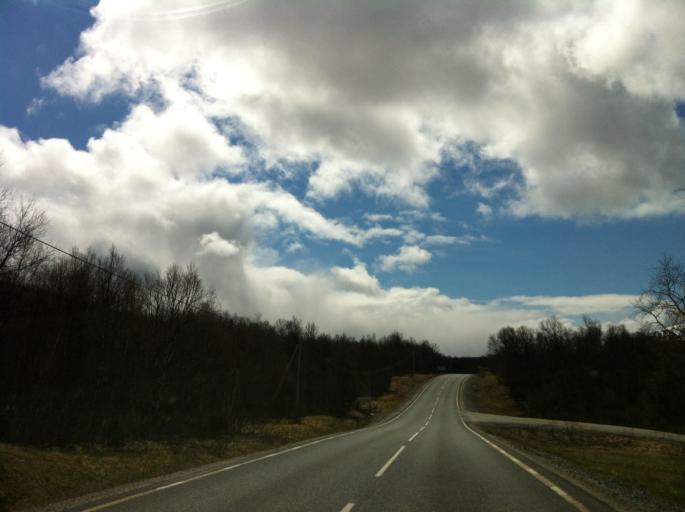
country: NO
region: Sor-Trondelag
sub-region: Tydal
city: Aas
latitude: 62.6658
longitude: 12.4296
